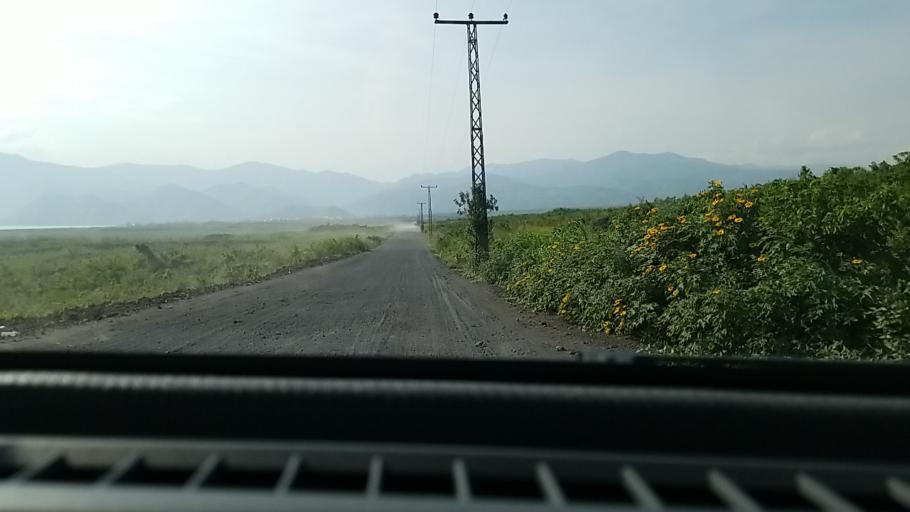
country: CD
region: Nord Kivu
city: Sake
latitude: -1.5901
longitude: 29.0958
